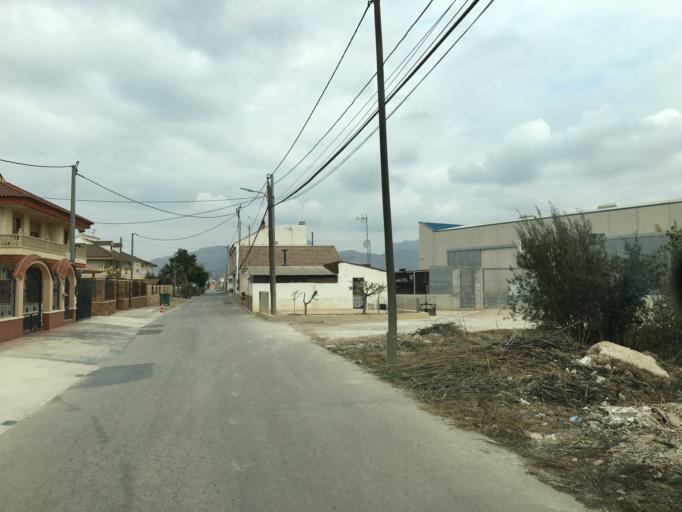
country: ES
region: Murcia
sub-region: Murcia
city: Beniel
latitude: 38.0349
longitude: -0.9851
